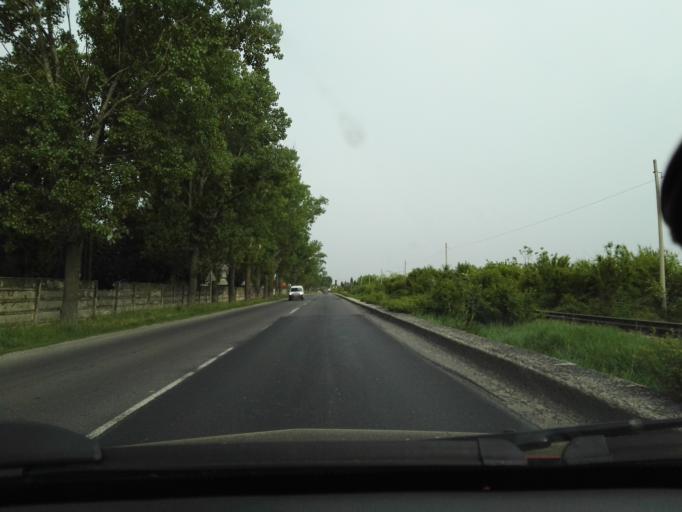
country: RO
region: Ilfov
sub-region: Comuna Magurele
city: Magurele
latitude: 44.3636
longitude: 26.0238
